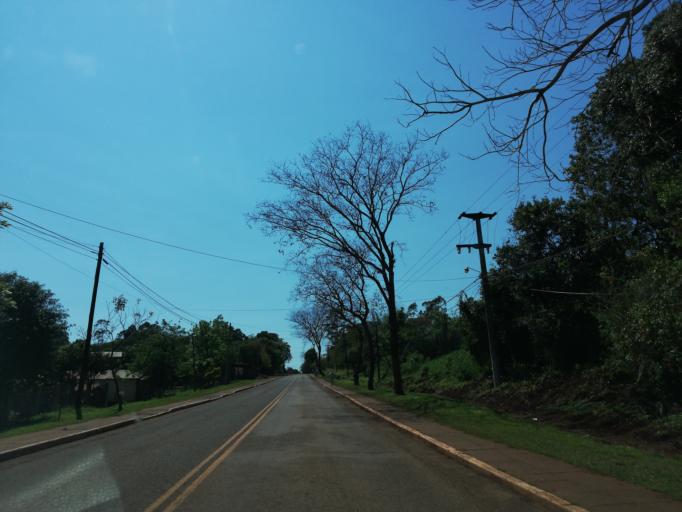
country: AR
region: Misiones
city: Puerto Eldorado
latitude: -26.4113
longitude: -54.6832
